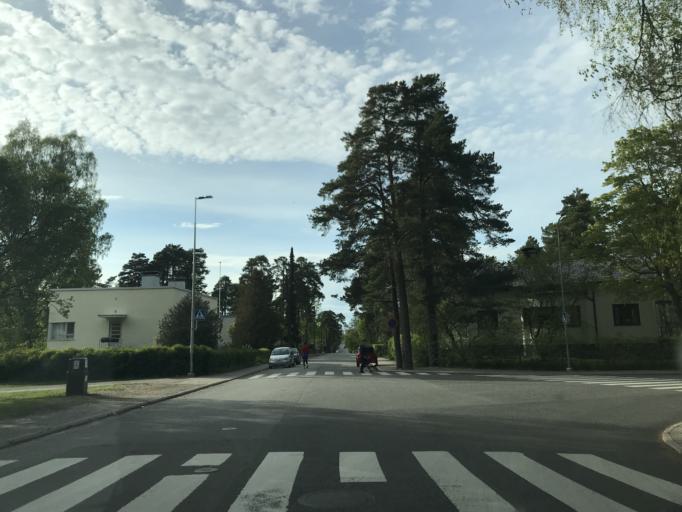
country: FI
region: Varsinais-Suomi
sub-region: Turku
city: Turku
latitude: 60.4363
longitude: 22.3019
